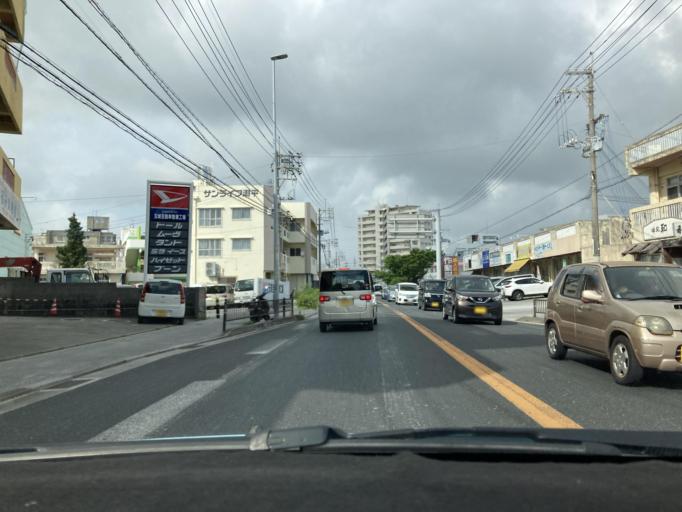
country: JP
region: Okinawa
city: Itoman
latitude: 26.1444
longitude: 127.6730
